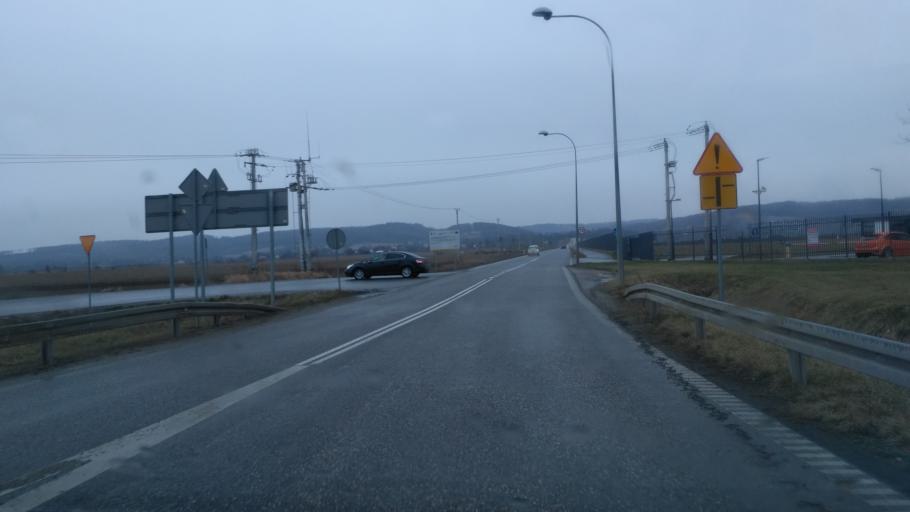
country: PL
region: Subcarpathian Voivodeship
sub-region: Powiat debicki
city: Brzeznica
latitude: 50.0748
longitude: 21.4683
